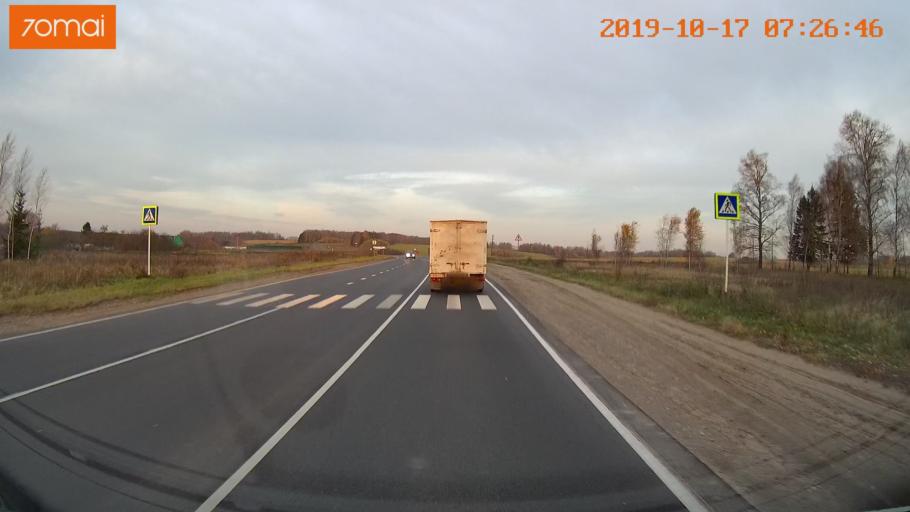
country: RU
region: Ivanovo
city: Gavrilov Posad
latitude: 56.3595
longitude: 40.0893
